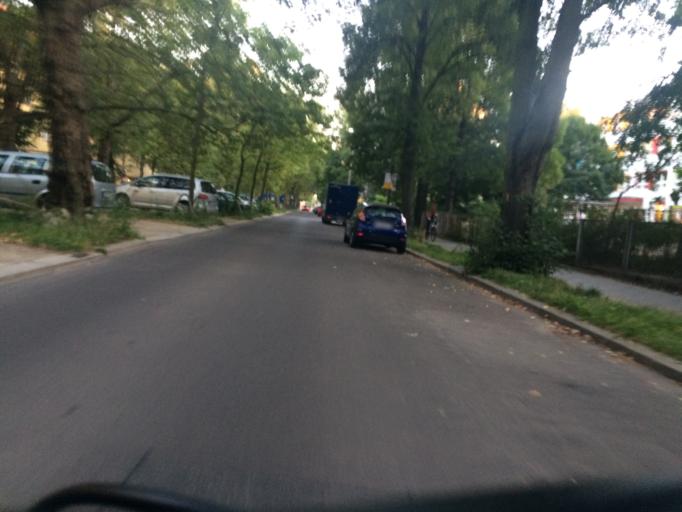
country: DE
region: Berlin
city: Heinersdorf
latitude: 52.5657
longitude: 13.4207
